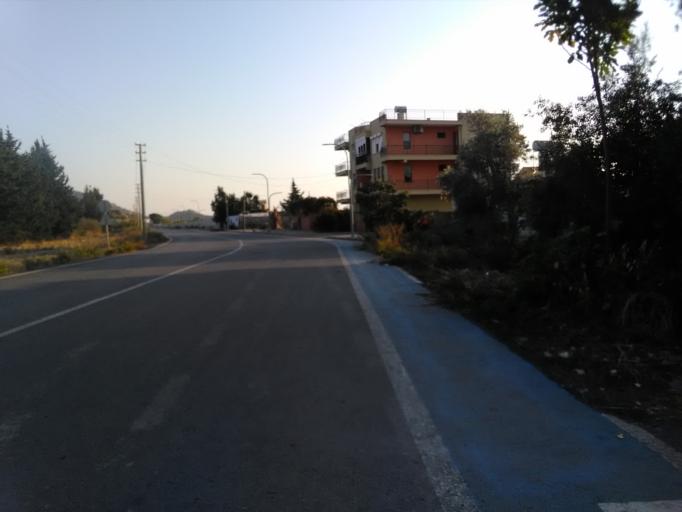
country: TR
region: Antalya
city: Gazipasa
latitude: 36.2543
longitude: 32.2911
